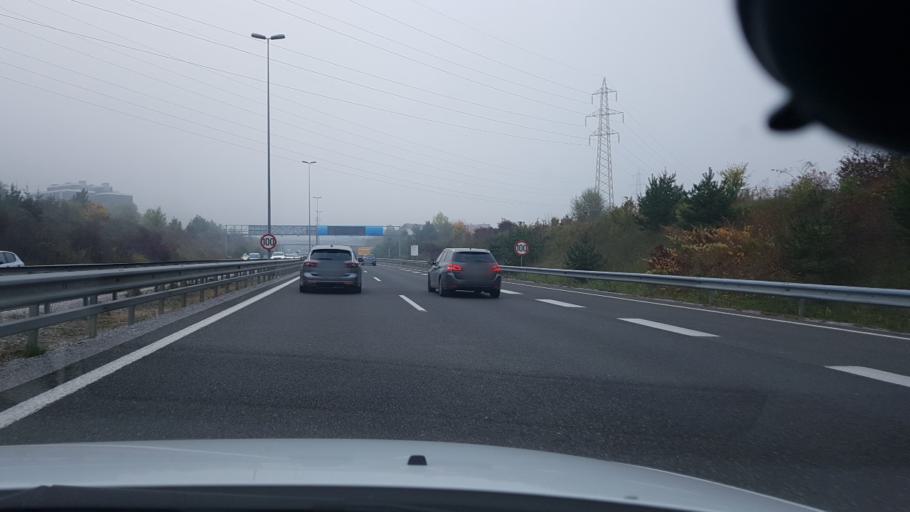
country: SI
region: Ljubljana
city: Ljubljana
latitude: 46.0791
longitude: 14.4604
